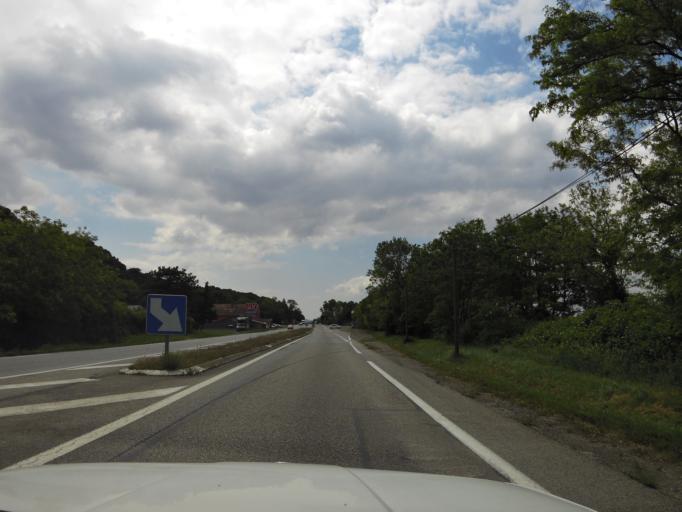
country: FR
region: Rhone-Alpes
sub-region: Departement de la Drome
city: Savasse
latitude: 44.6053
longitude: 4.7542
